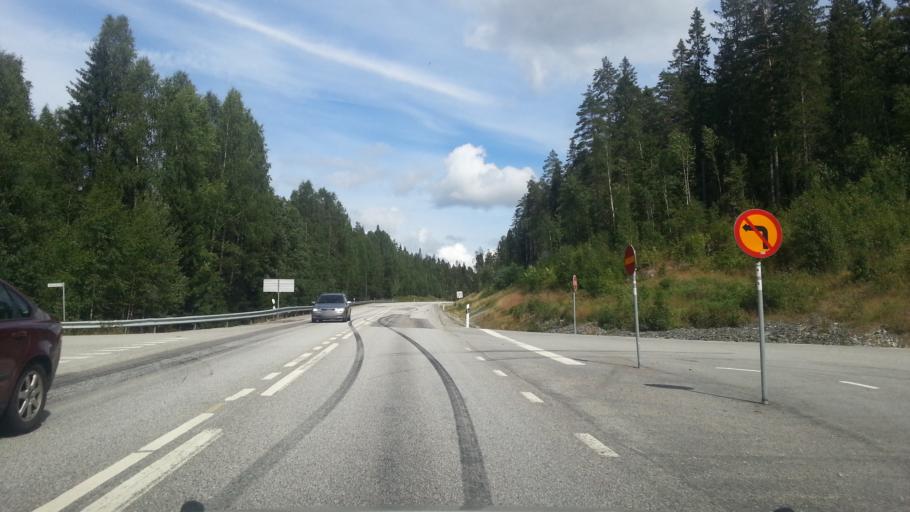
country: SE
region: Vaestmanland
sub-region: Skinnskattebergs Kommun
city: Skinnskatteberg
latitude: 59.8260
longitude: 15.5331
